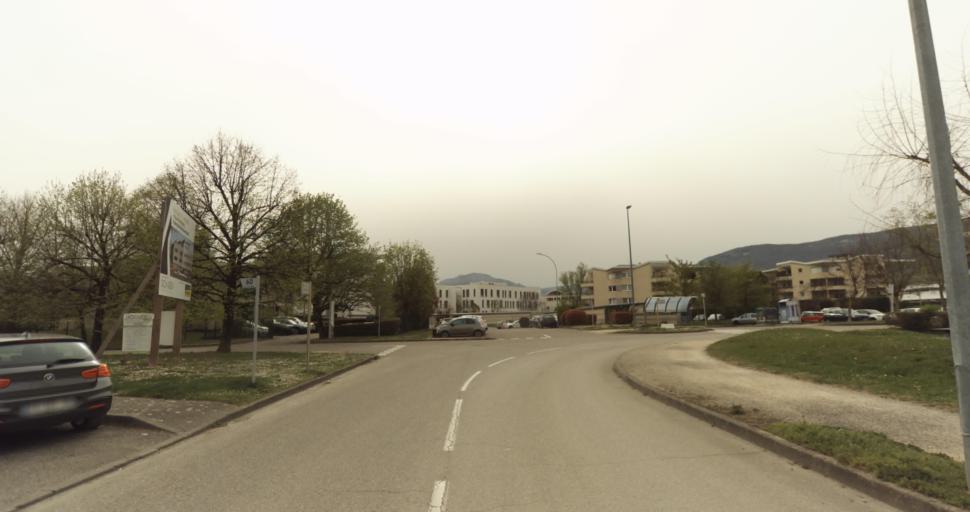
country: FR
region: Rhone-Alpes
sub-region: Departement de l'Isere
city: Montbonnot-Saint-Martin
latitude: 45.2172
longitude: 5.8096
